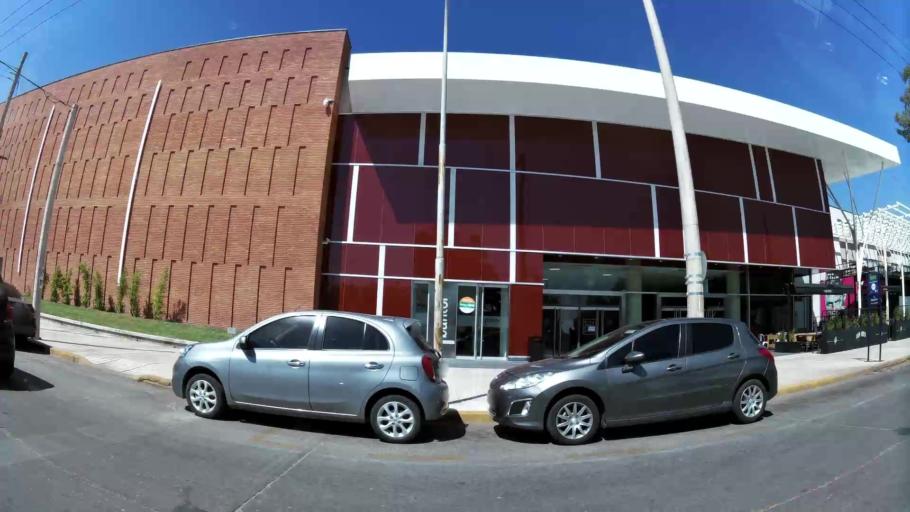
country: AR
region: Cordoba
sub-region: Departamento de Capital
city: Cordoba
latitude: -31.4118
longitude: -64.2424
